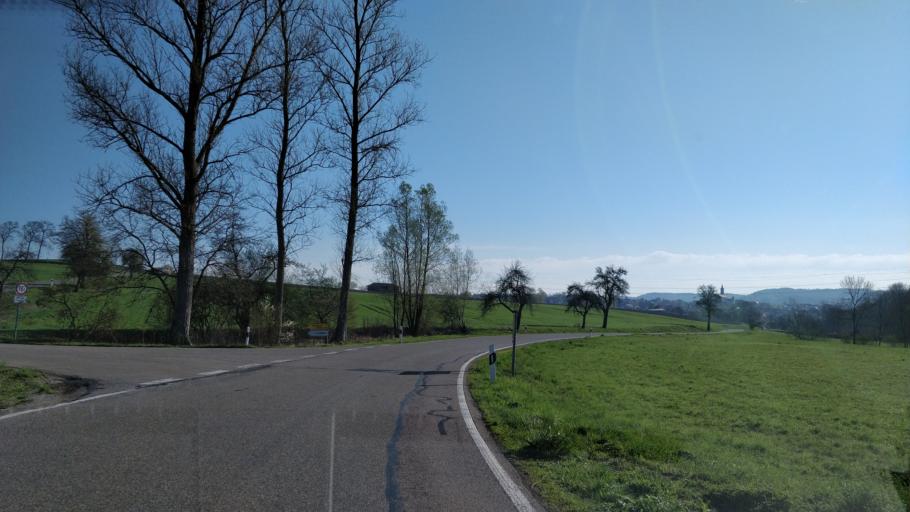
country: DE
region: Baden-Wuerttemberg
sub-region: Regierungsbezirk Stuttgart
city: Michelbach an der Bilz
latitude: 49.0508
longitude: 9.7128
